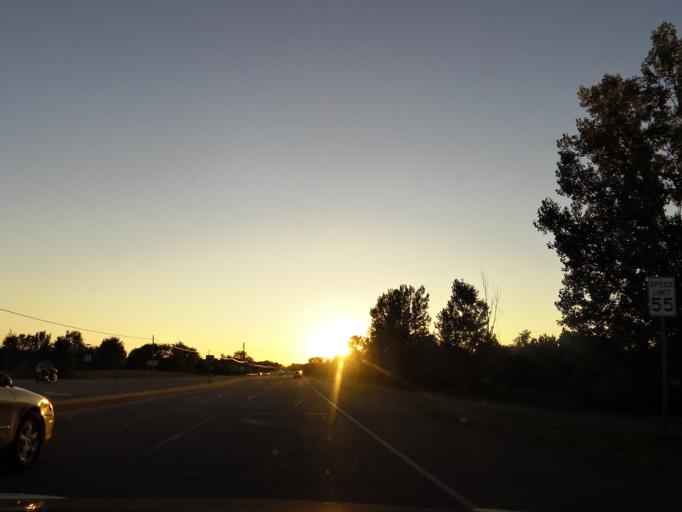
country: US
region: Minnesota
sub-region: Washington County
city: Oakdale
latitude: 44.9636
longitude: -92.9347
